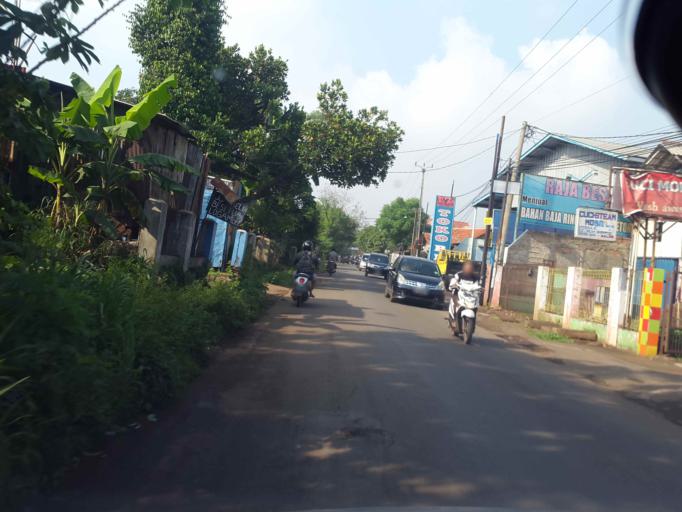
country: ID
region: West Java
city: Cileungsir
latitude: -6.3799
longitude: 106.9927
